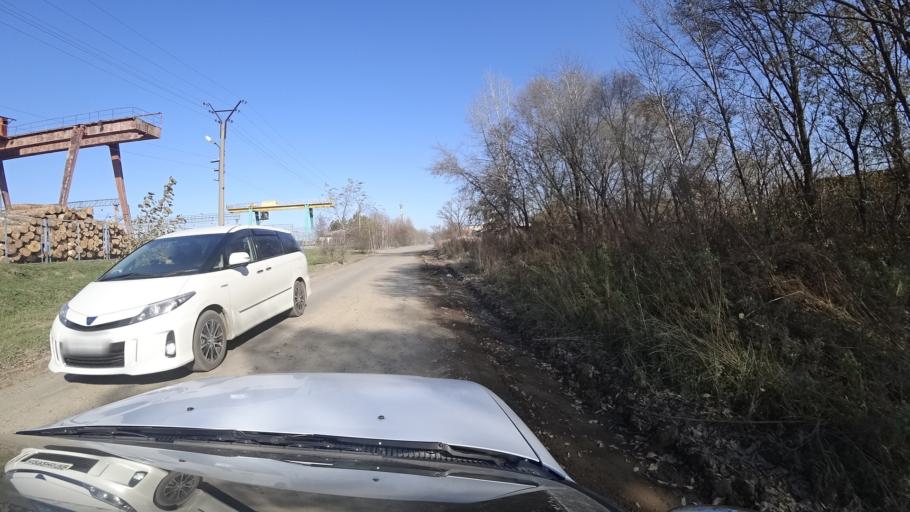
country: RU
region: Primorskiy
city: Dal'nerechensk
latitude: 45.9332
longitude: 133.7194
